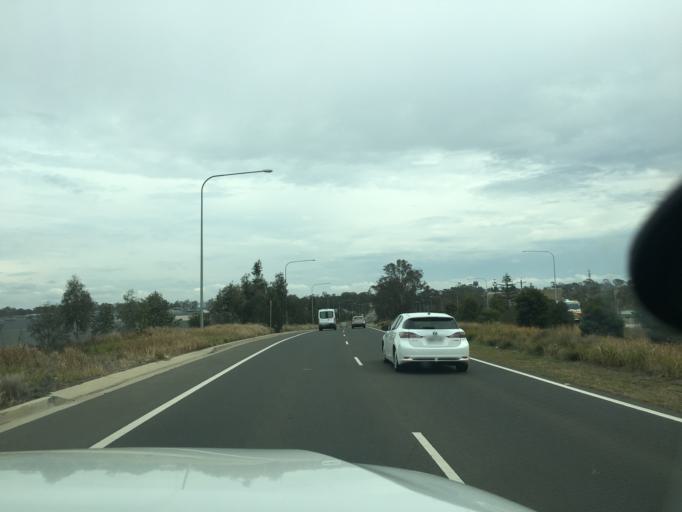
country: AU
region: New South Wales
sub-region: Campbelltown Municipality
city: Denham Court
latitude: -33.9770
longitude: 150.8087
